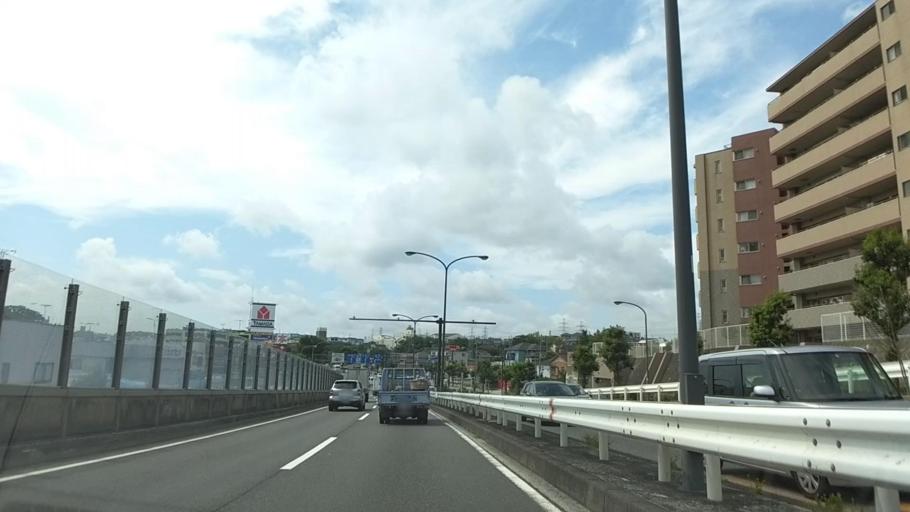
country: JP
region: Kanagawa
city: Yokohama
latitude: 35.4153
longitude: 139.5593
